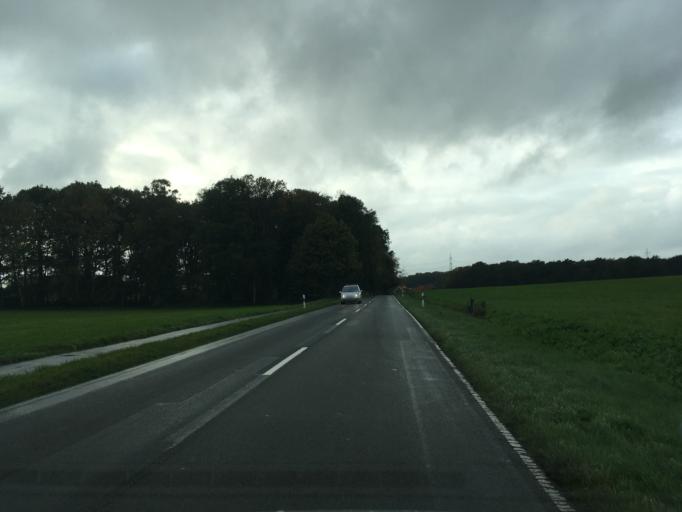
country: DE
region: North Rhine-Westphalia
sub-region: Regierungsbezirk Munster
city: Heiden
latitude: 51.8234
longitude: 6.9668
